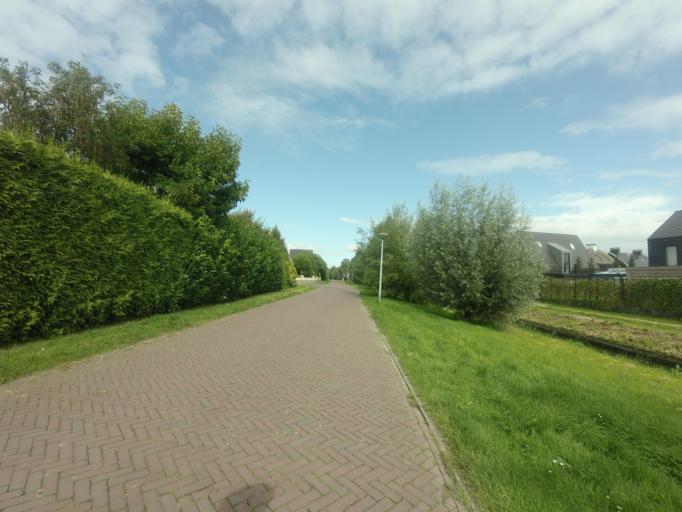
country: NL
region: North Holland
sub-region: Gemeente Huizen
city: Huizen
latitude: 52.2950
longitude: 5.2831
